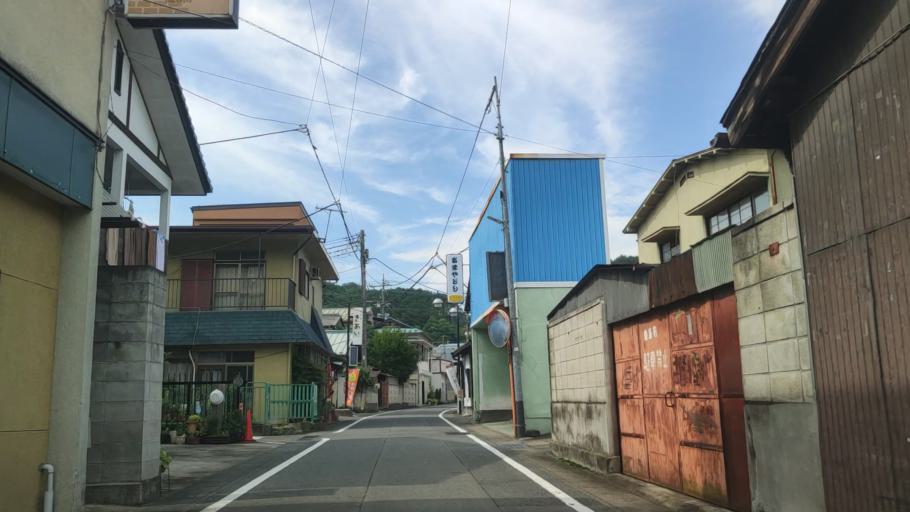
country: JP
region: Gunma
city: Tomioka
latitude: 36.2109
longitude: 138.7845
